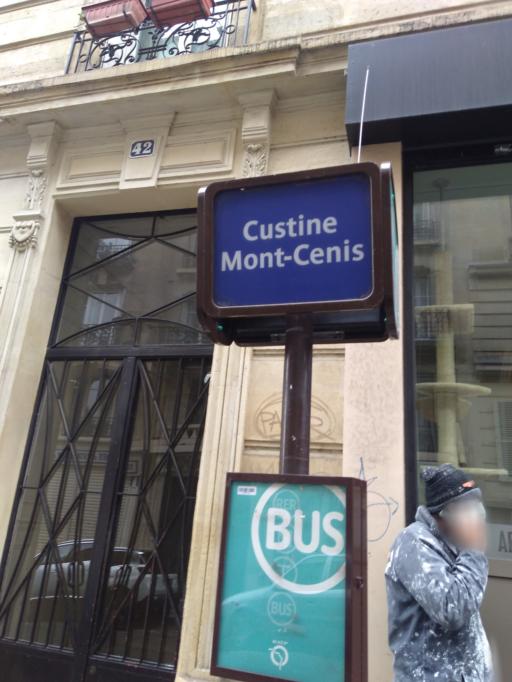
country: FR
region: Ile-de-France
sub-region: Paris
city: Saint-Ouen
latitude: 48.8901
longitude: 2.3432
